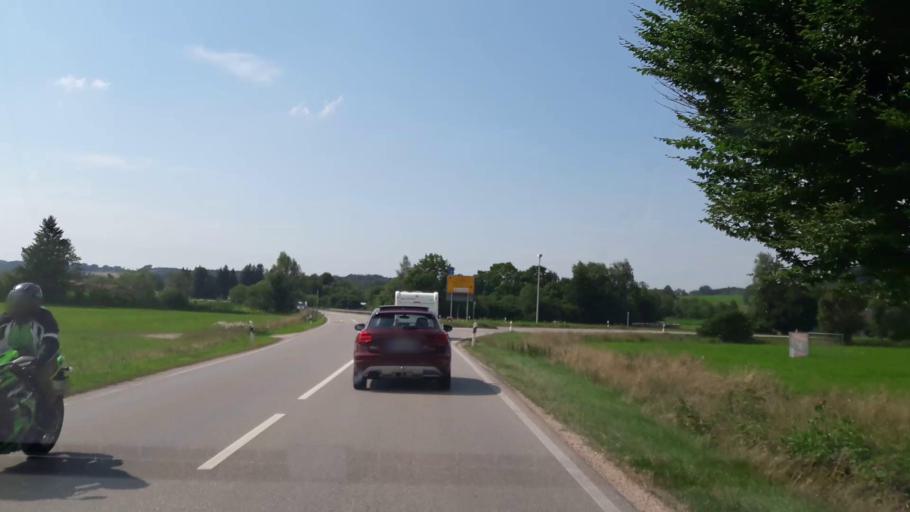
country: DE
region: Bavaria
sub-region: Upper Bavaria
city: Teisendorf
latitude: 47.8474
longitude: 12.8116
